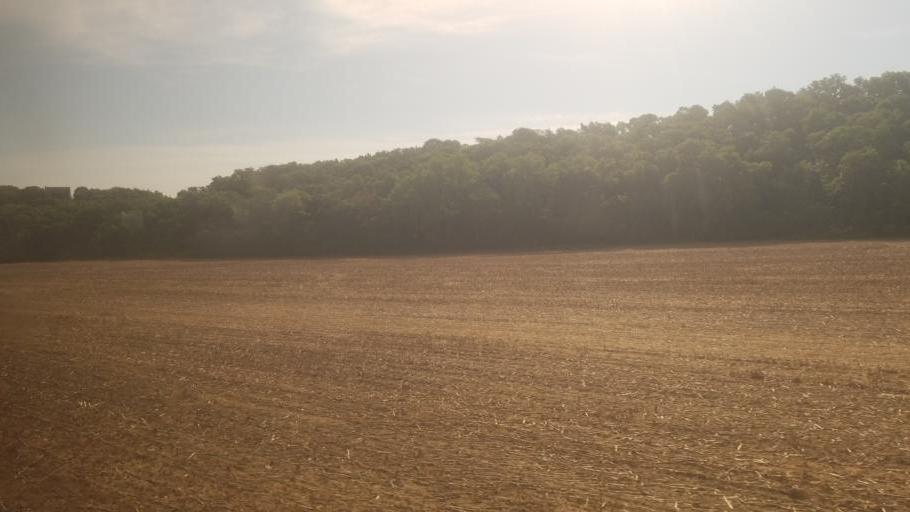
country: US
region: Kansas
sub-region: Wyandotte County
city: Bonner Springs
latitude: 39.0277
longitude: -94.8789
